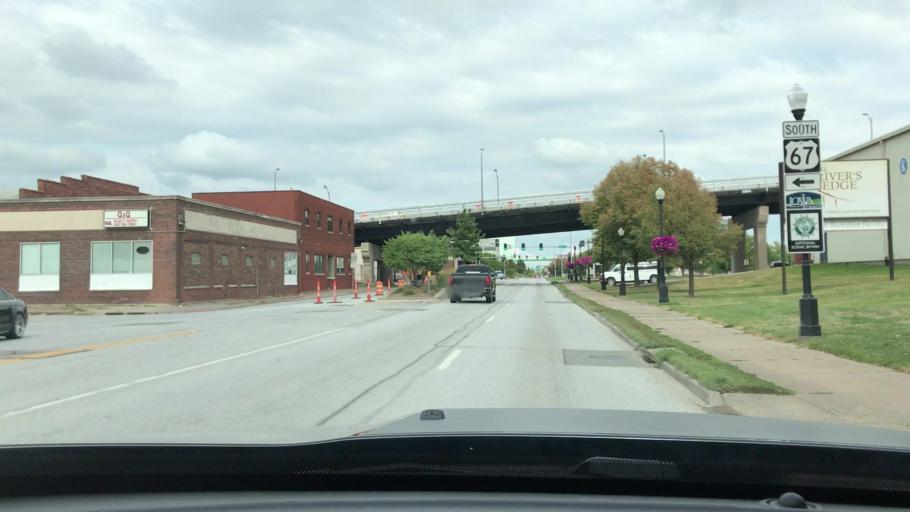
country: US
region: Iowa
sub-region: Scott County
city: Davenport
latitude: 41.5201
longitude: -90.5848
